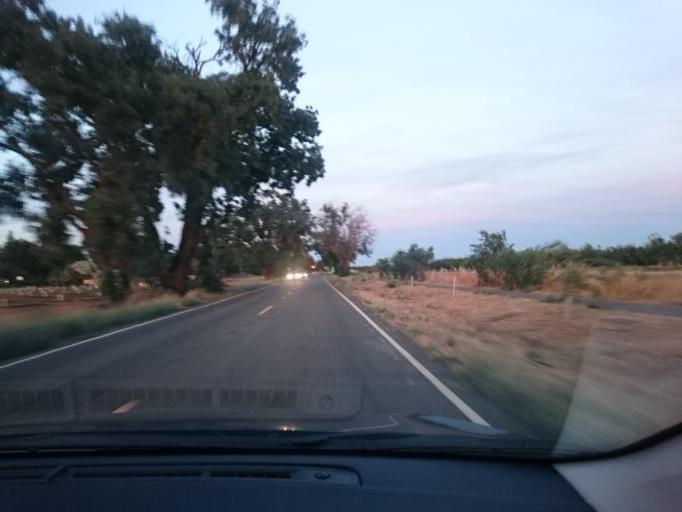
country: US
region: California
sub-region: Yolo County
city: Davis
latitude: 38.5468
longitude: -121.7954
